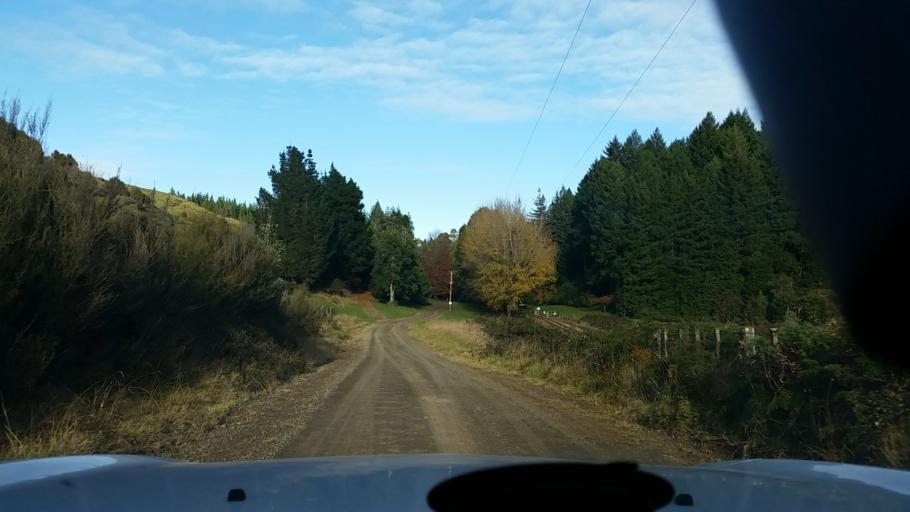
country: NZ
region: Hawke's Bay
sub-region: Napier City
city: Napier
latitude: -39.2413
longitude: 176.8099
